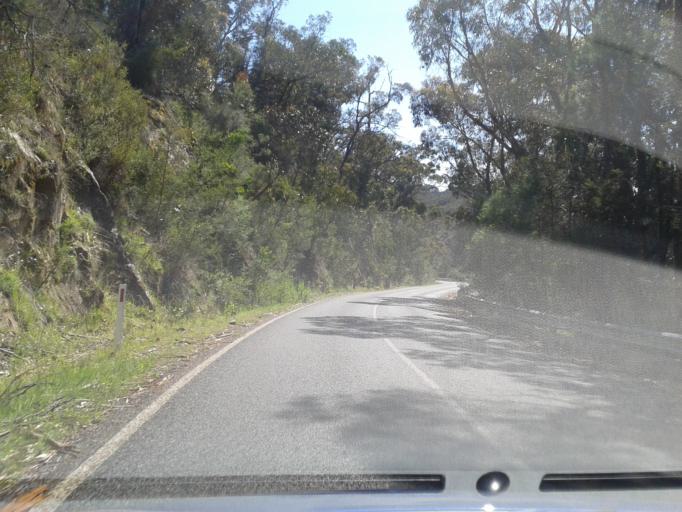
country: AU
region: Victoria
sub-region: Northern Grampians
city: Stawell
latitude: -37.1399
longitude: 142.5067
